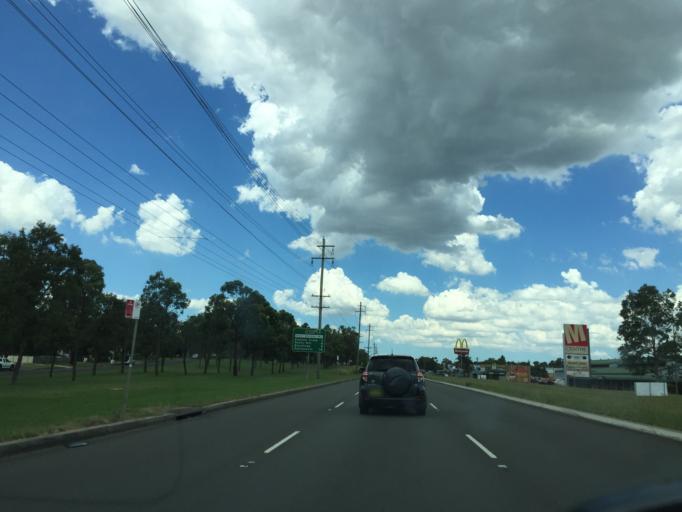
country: AU
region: New South Wales
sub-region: Blacktown
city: Mount Druitt
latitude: -33.7799
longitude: 150.8173
